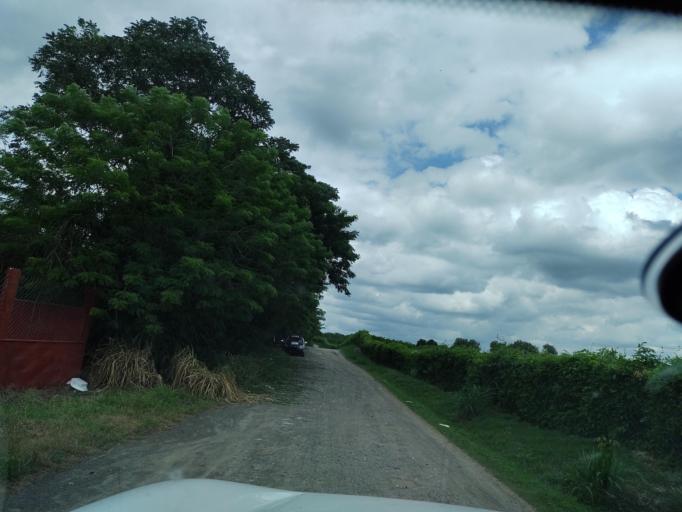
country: MX
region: Veracruz
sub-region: Martinez de la Torre
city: El Progreso
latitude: 20.1112
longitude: -97.0202
